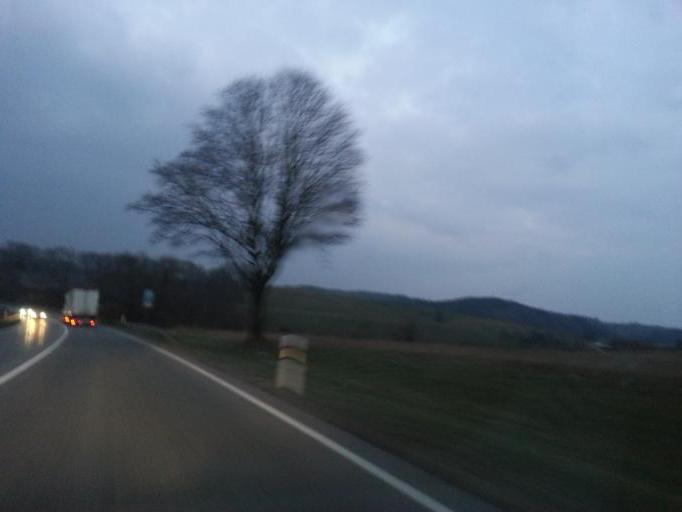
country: DE
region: Baden-Wuerttemberg
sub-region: Tuebingen Region
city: Bad Waldsee
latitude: 47.9082
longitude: 9.7611
